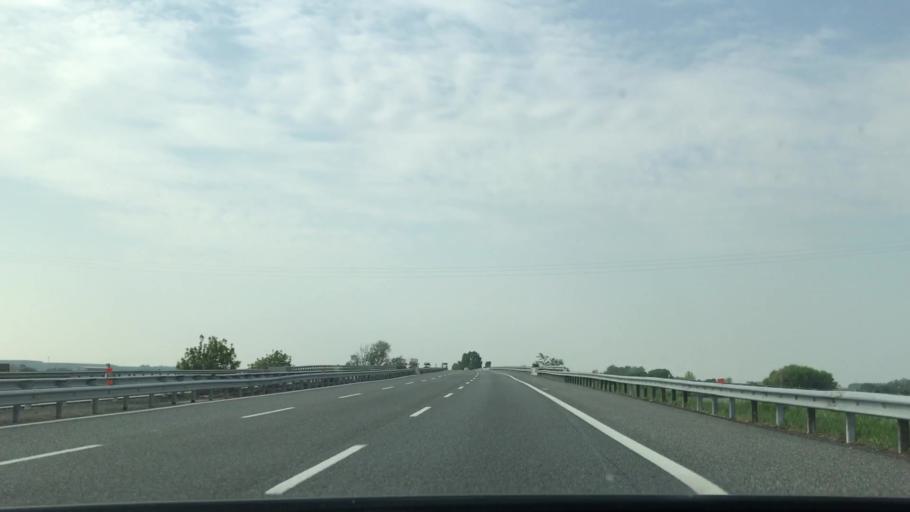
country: IT
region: Piedmont
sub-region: Provincia di Vercelli
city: Borgo Vercelli
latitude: 45.3335
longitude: 8.4717
